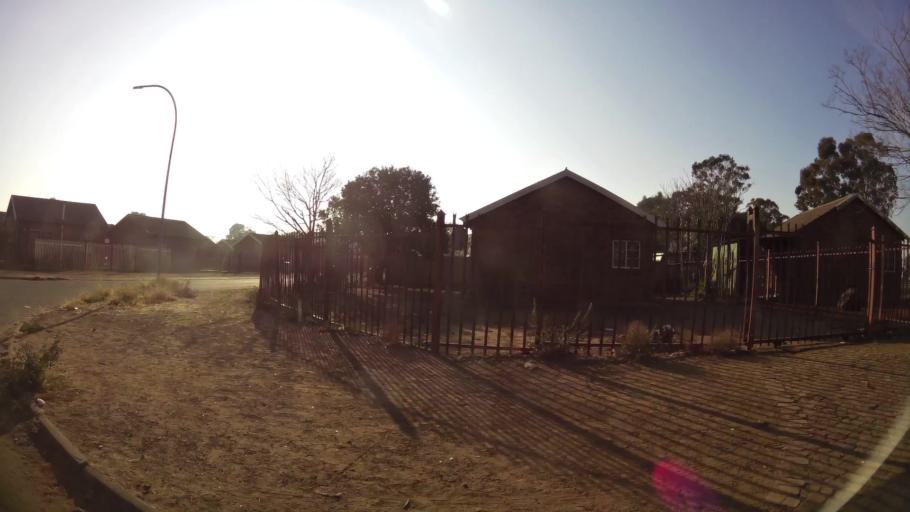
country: ZA
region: Orange Free State
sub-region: Mangaung Metropolitan Municipality
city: Bloemfontein
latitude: -29.1562
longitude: 26.2160
